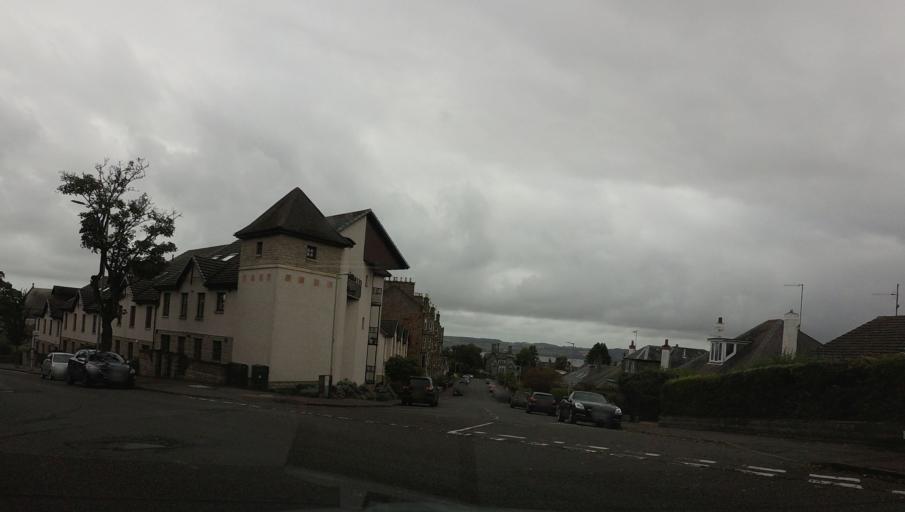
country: GB
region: Scotland
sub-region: Dundee City
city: Dundee
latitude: 56.4591
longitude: -2.9996
